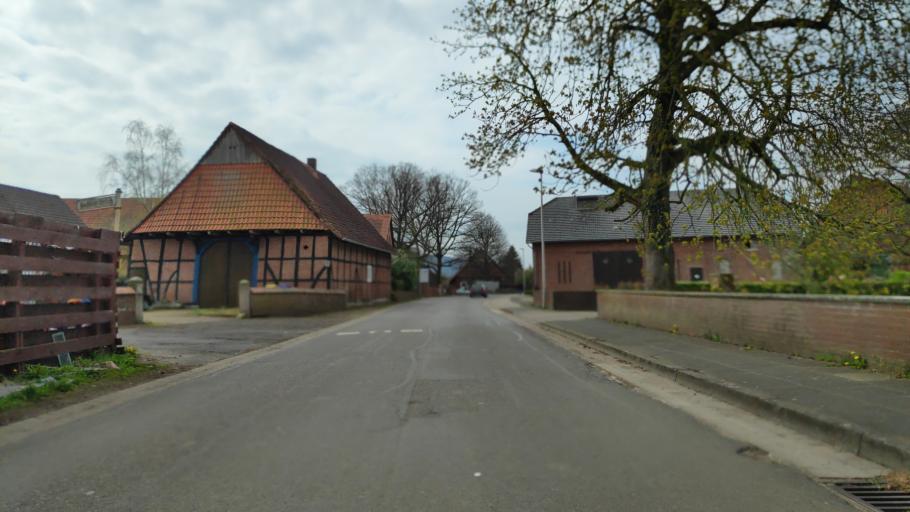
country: DE
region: North Rhine-Westphalia
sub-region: Regierungsbezirk Detmold
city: Minden
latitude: 52.2687
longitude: 8.9496
